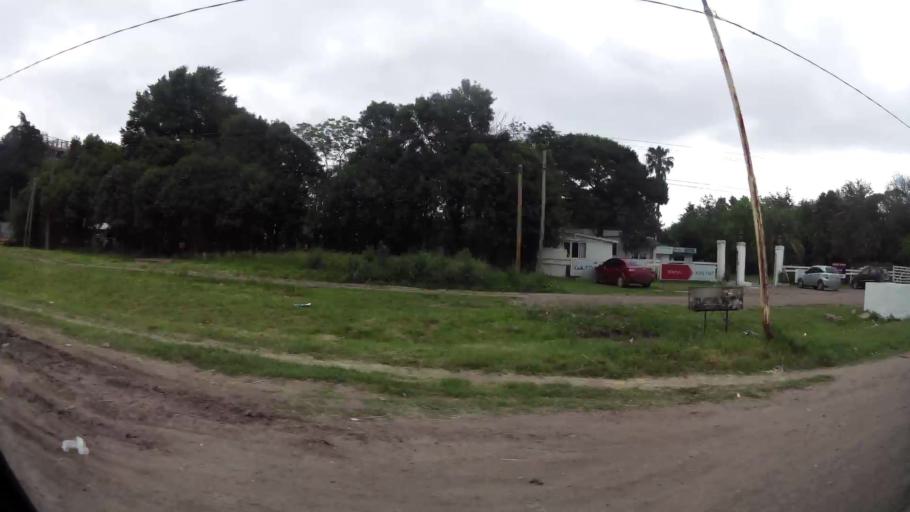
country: AR
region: Buenos Aires
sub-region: Partido de Ezeiza
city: Ezeiza
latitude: -34.8821
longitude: -58.5043
